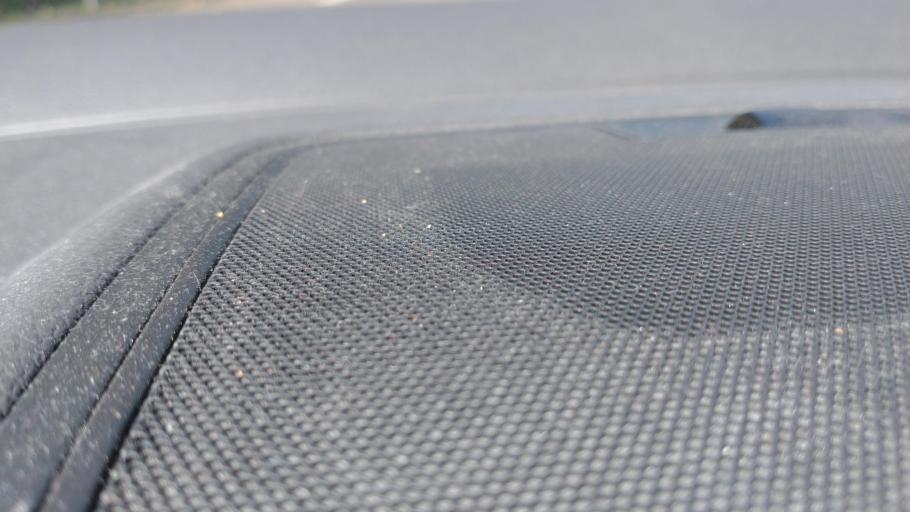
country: DE
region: Baden-Wuerttemberg
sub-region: Tuebingen Region
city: Kressbronn am Bodensee
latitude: 47.5970
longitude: 9.5940
